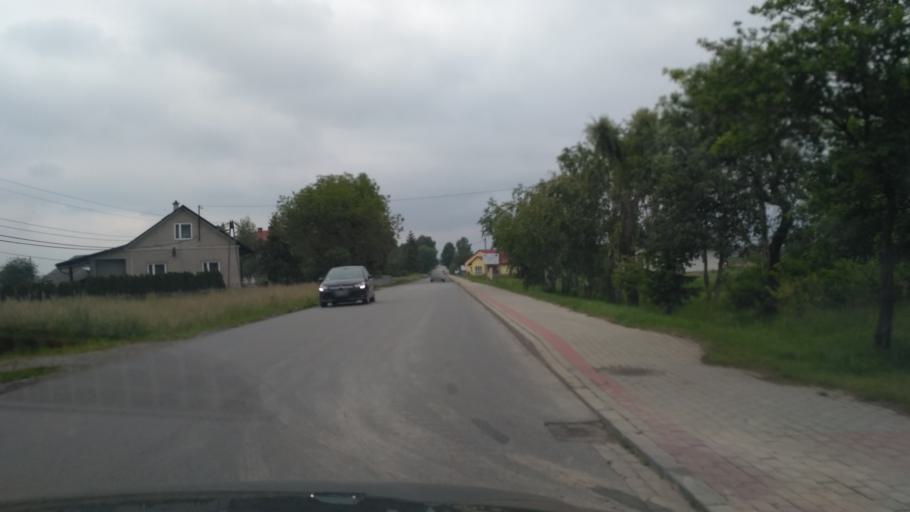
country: PL
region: Subcarpathian Voivodeship
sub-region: Powiat ropczycko-sedziszowski
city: Sedziszow Malopolski
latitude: 50.0833
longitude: 21.6699
